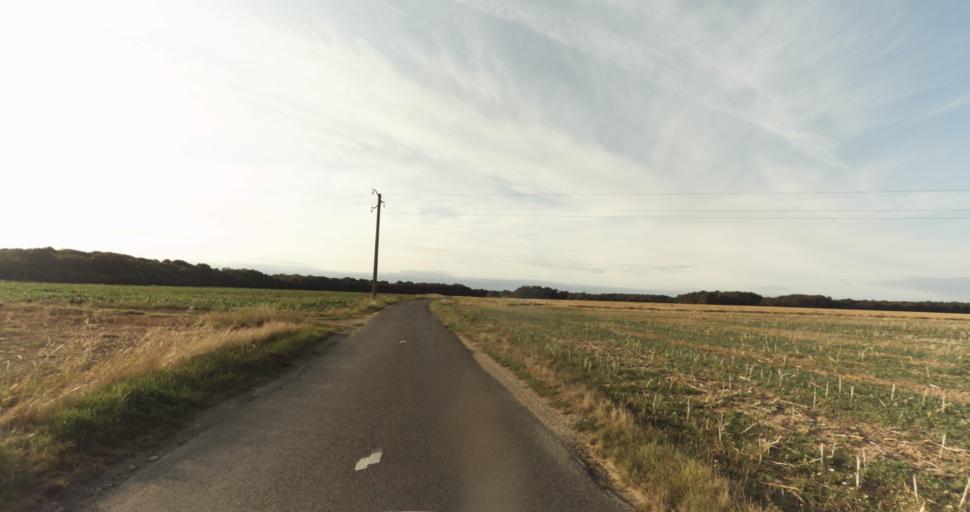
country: FR
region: Haute-Normandie
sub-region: Departement de l'Eure
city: Marcilly-sur-Eure
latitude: 48.8261
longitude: 1.2881
